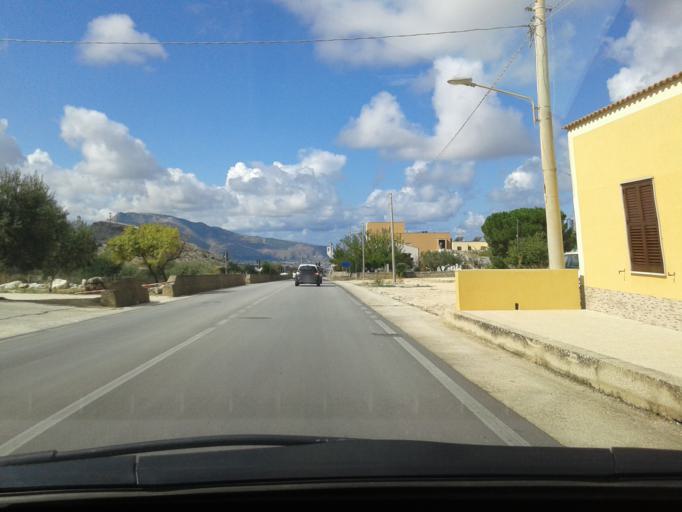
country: IT
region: Sicily
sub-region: Trapani
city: Custonaci
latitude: 38.0767
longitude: 12.6964
